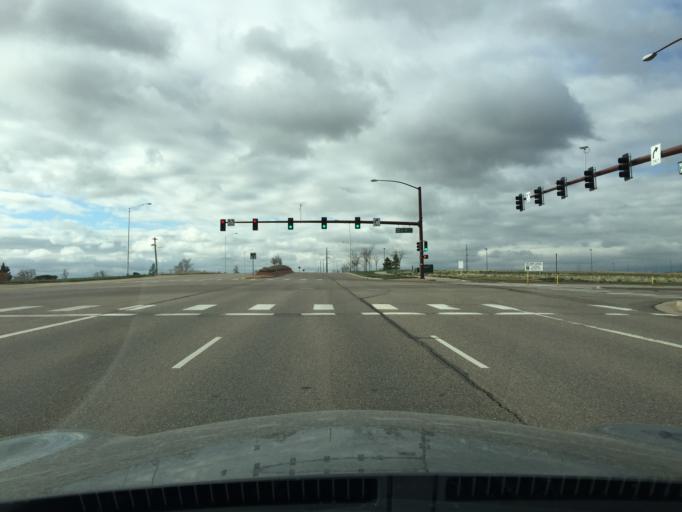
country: US
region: Colorado
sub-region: Boulder County
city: Erie
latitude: 39.9905
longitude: -104.9784
